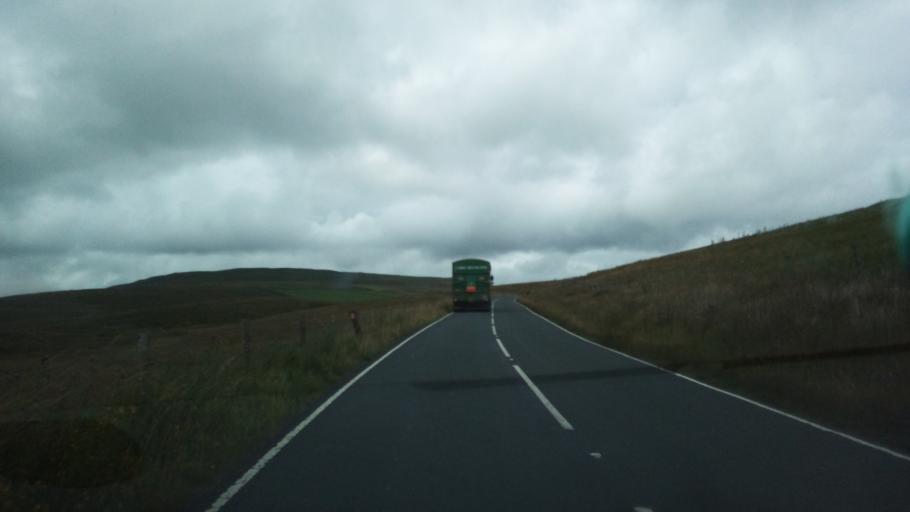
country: GB
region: England
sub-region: North Yorkshire
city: Ingleton
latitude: 54.2410
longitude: -2.3161
